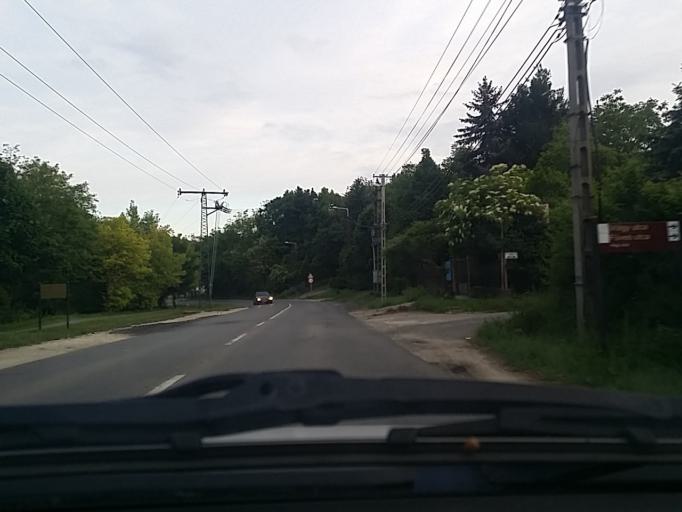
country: HU
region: Pest
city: Solymar
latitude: 47.5781
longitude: 18.9382
